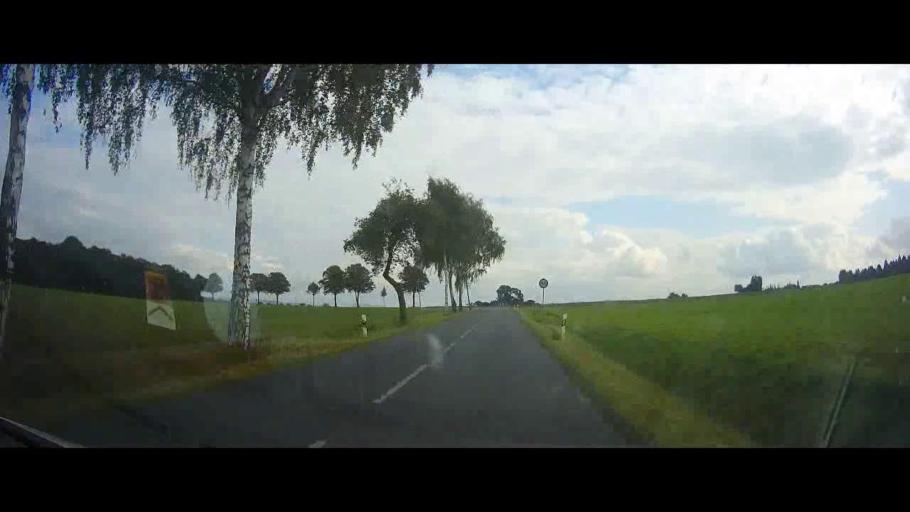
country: DE
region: Lower Saxony
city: Rosdorf
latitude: 51.5586
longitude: 9.8495
